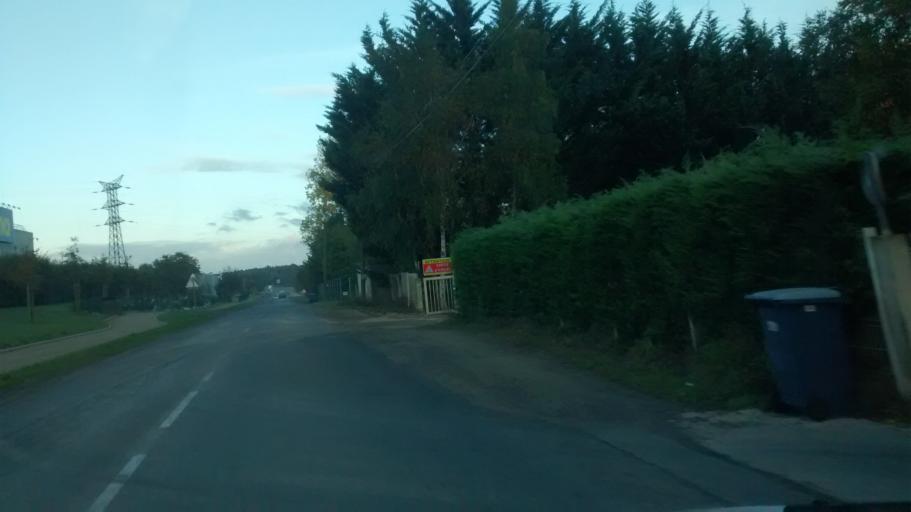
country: FR
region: Brittany
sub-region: Departement d'Ille-et-Vilaine
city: La Chapelle-des-Fougeretz
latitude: 48.2013
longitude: -1.7239
